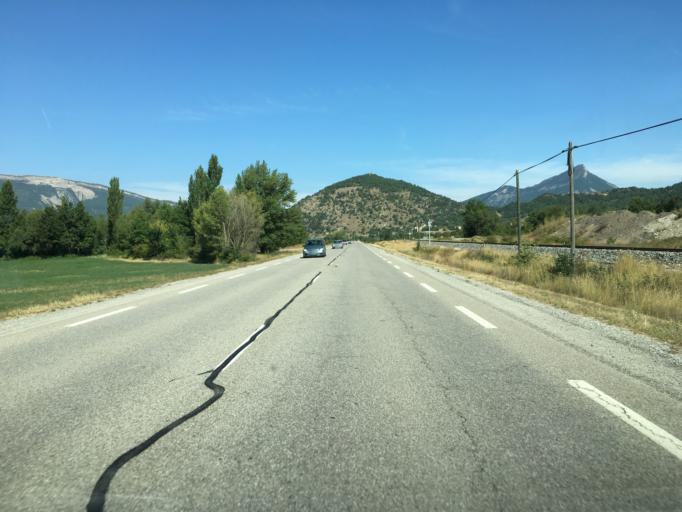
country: FR
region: Provence-Alpes-Cote d'Azur
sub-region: Departement des Hautes-Alpes
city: Serres
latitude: 44.3673
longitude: 5.7557
